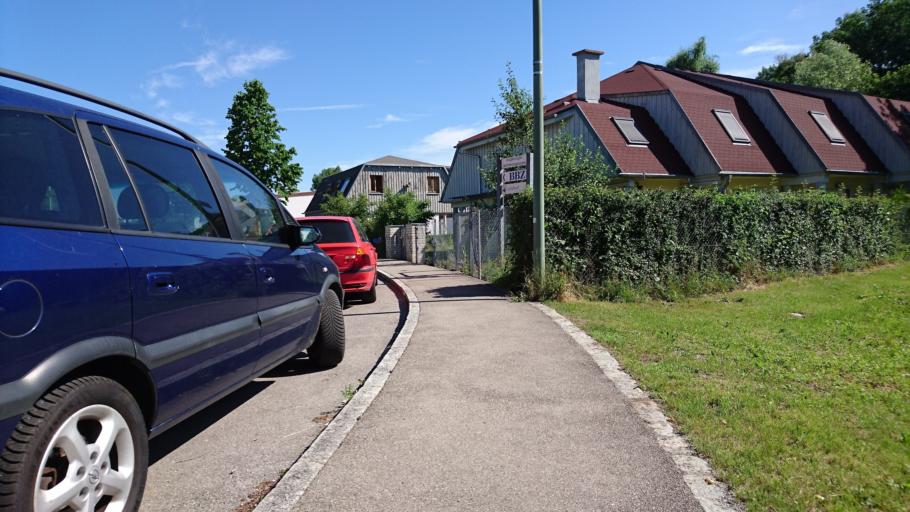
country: DE
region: Bavaria
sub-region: Swabia
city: Gersthofen
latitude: 48.4030
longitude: 10.8814
